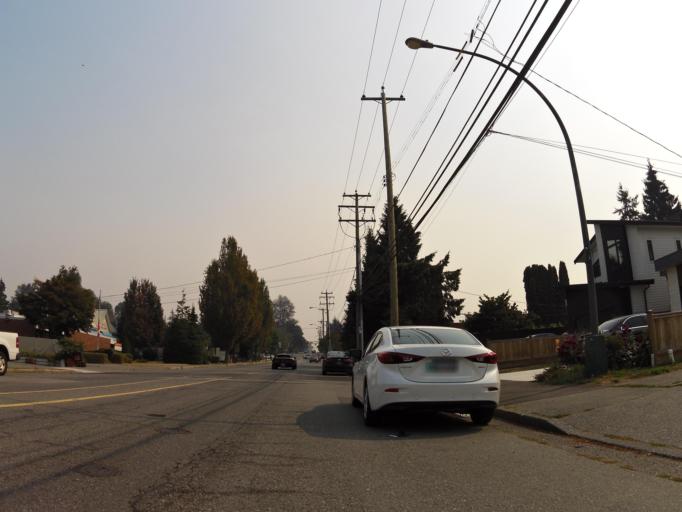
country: CA
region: British Columbia
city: Delta
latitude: 49.1560
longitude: -122.9149
